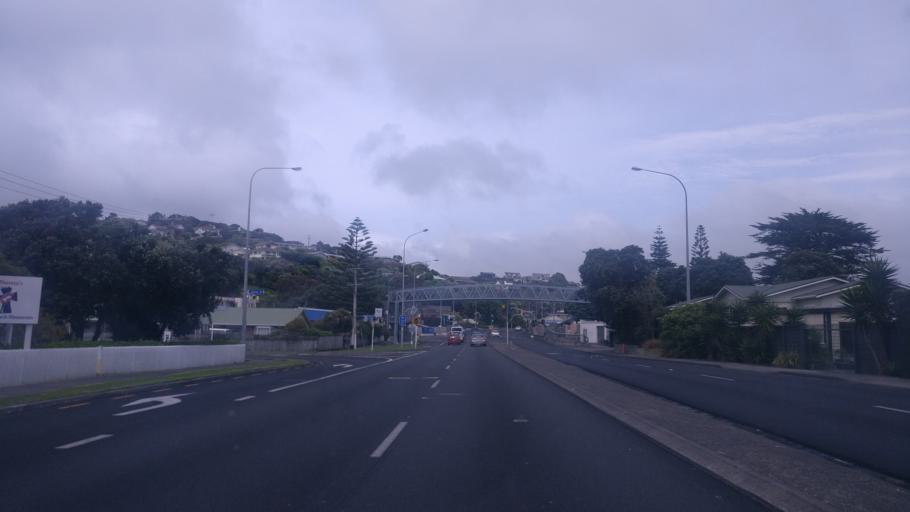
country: NZ
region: Wellington
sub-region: Porirua City
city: Porirua
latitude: -41.0841
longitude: 174.8688
